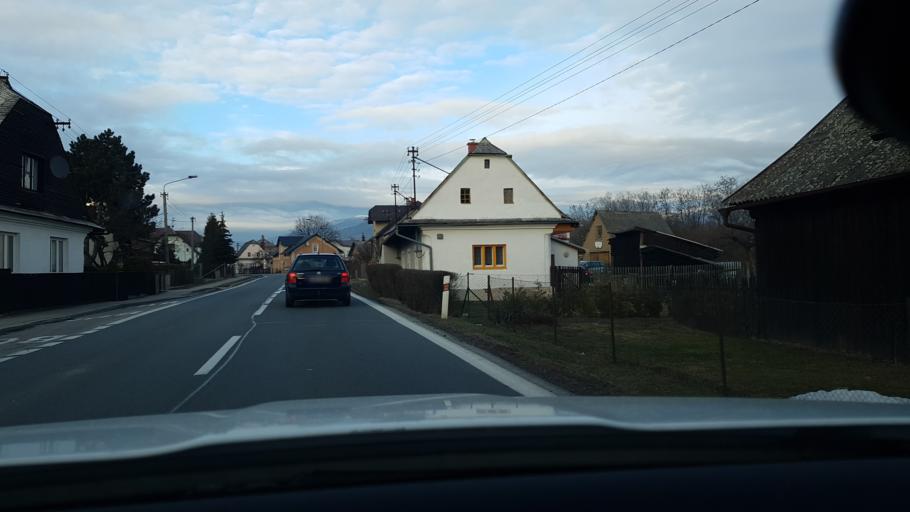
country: CZ
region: Olomoucky
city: Rapotin
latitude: 50.0069
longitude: 17.0277
